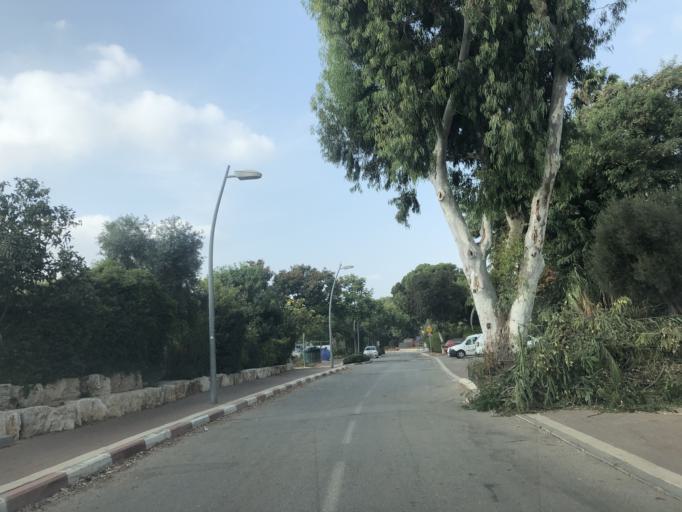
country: IL
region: Central District
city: Rosh Ha'Ayin
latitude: 32.0819
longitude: 34.9360
